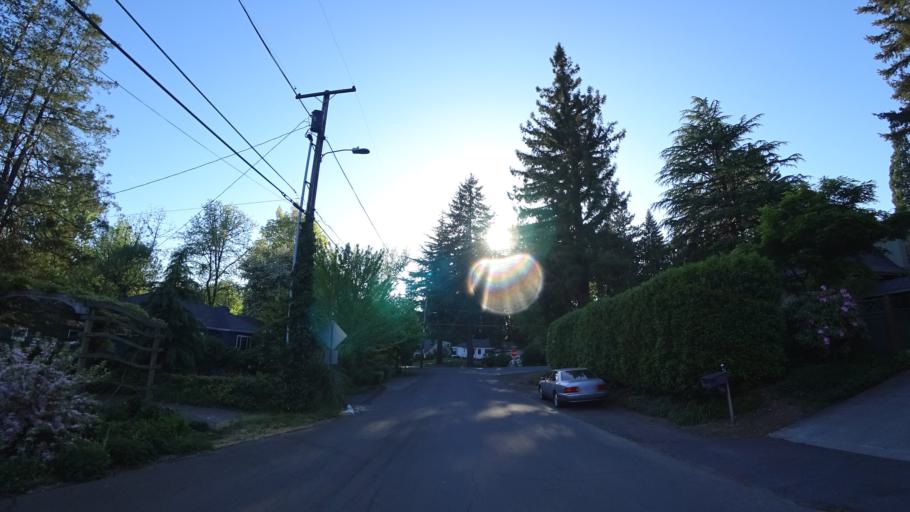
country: US
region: Oregon
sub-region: Washington County
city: West Slope
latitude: 45.4911
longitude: -122.7644
